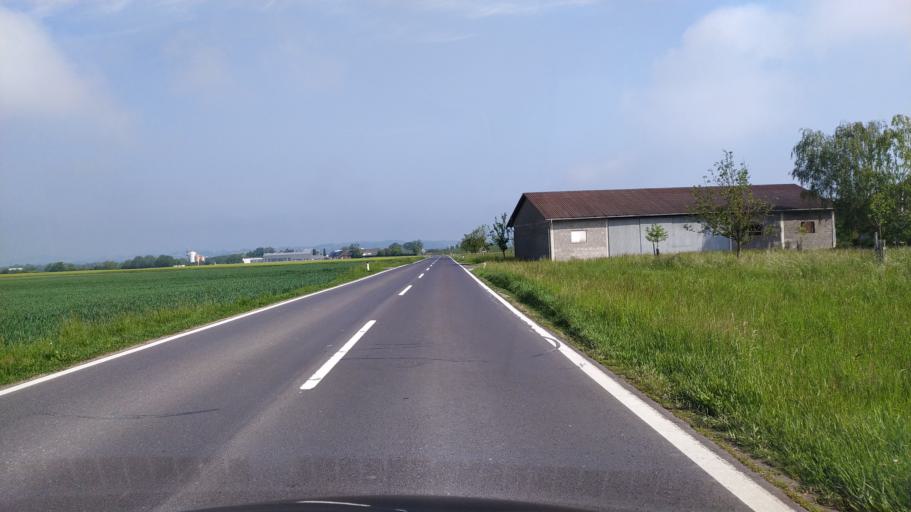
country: AT
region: Lower Austria
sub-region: Politischer Bezirk Amstetten
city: Ennsdorf
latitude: 48.2095
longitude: 14.5447
